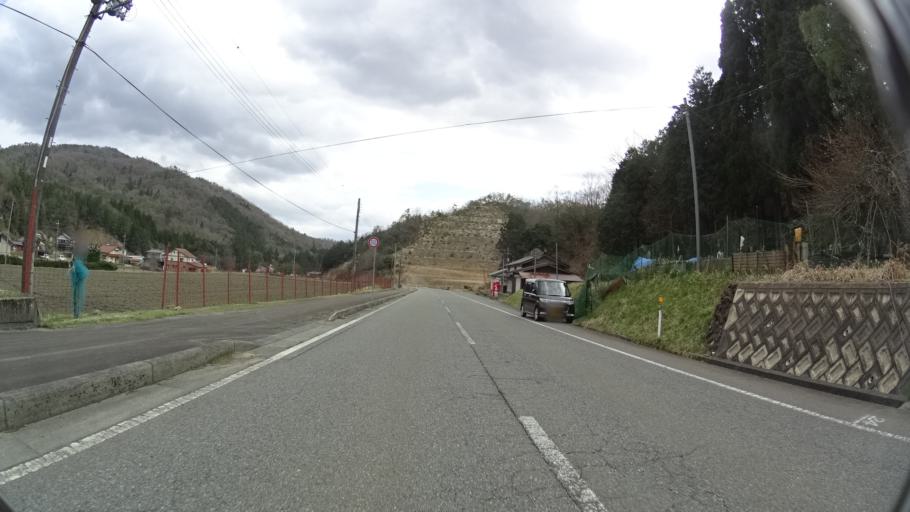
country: JP
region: Hyogo
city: Toyooka
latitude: 35.4847
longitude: 134.9238
